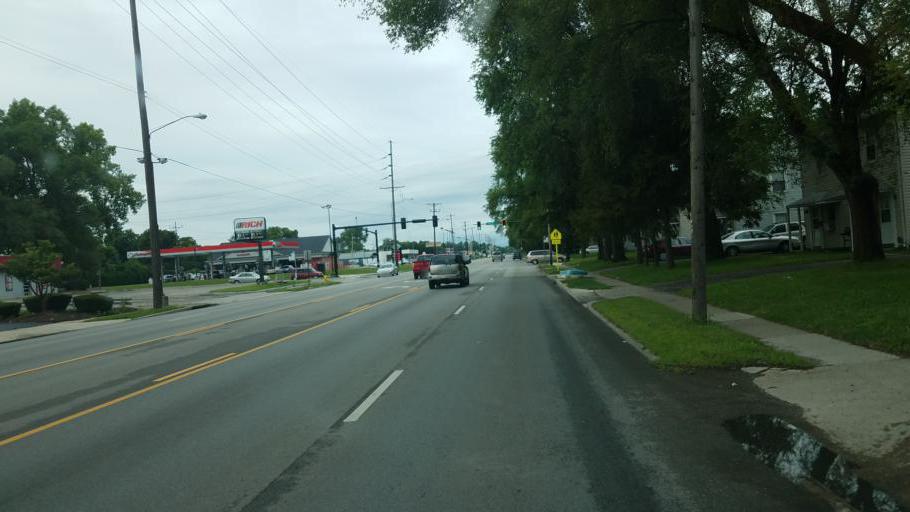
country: US
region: Ohio
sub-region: Franklin County
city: Whitehall
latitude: 39.9593
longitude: -82.8764
